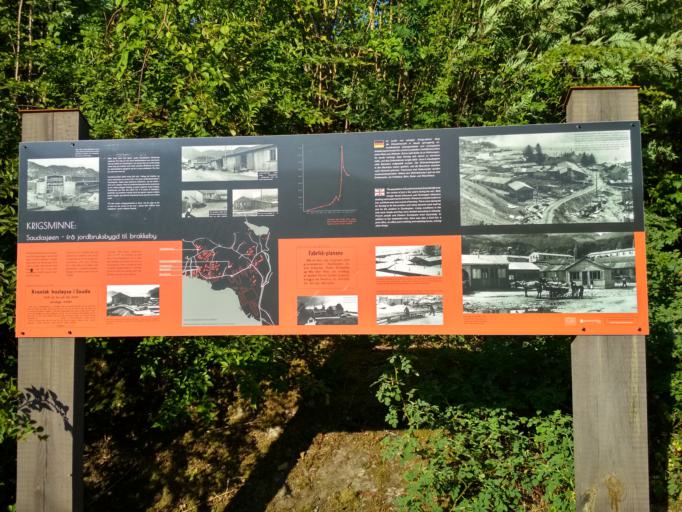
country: NO
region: Rogaland
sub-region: Sauda
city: Sauda
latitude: 59.6399
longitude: 6.3102
